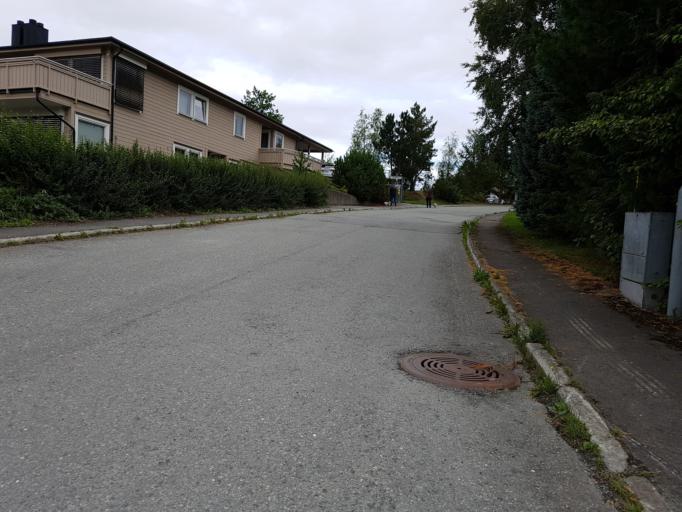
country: NO
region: Sor-Trondelag
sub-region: Trondheim
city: Trondheim
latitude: 63.3986
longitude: 10.4450
